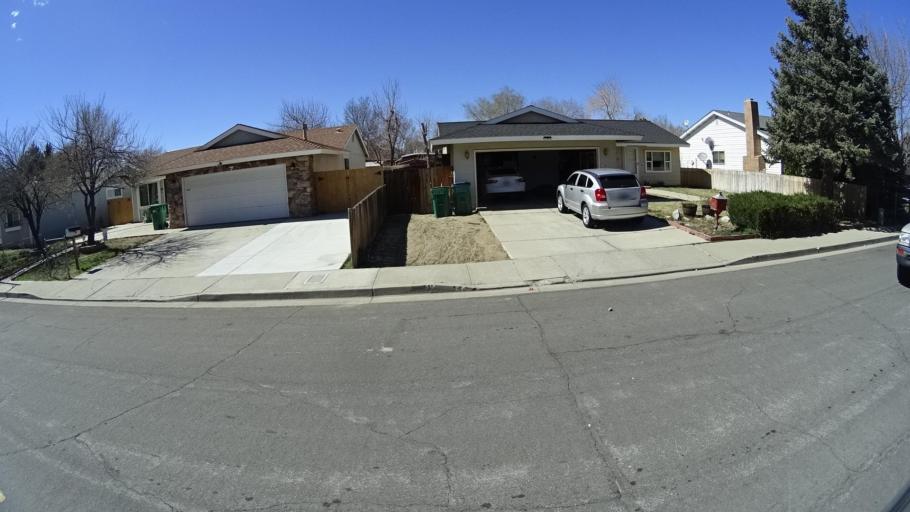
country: US
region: Nevada
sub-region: Washoe County
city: Sparks
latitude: 39.4845
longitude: -119.7557
